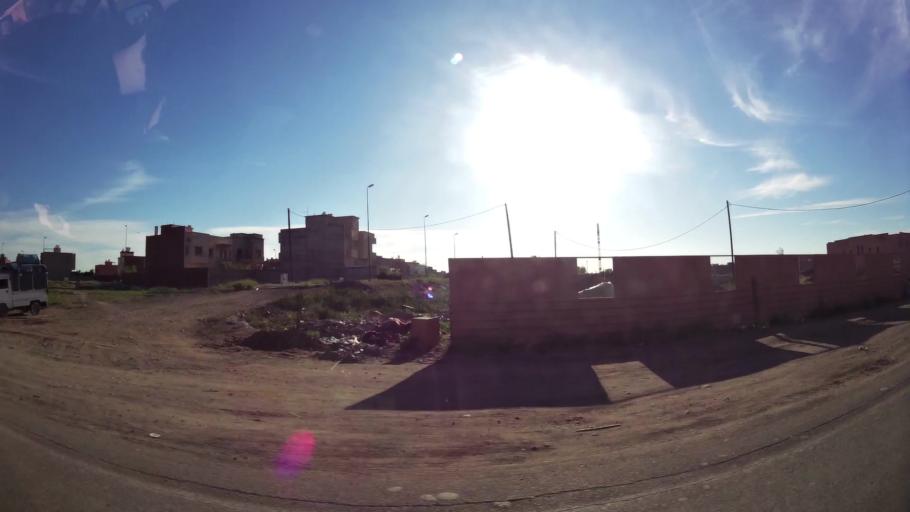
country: MA
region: Marrakech-Tensift-Al Haouz
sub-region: Marrakech
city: Marrakesh
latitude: 31.6782
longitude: -8.0597
